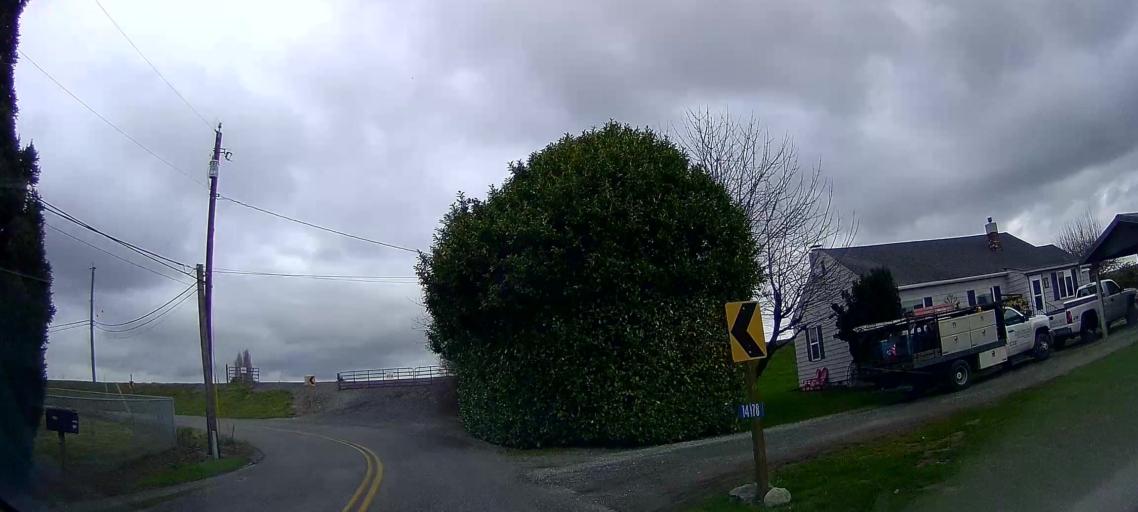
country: US
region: Washington
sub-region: Skagit County
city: Mount Vernon
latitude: 48.4461
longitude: -122.3574
